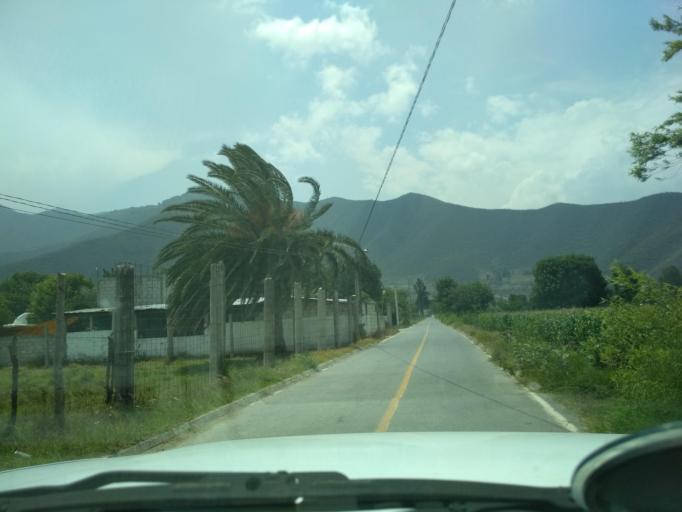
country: MX
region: Veracruz
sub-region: Nogales
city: Taza de Agua Ojo Zarco
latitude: 18.7727
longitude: -97.2155
